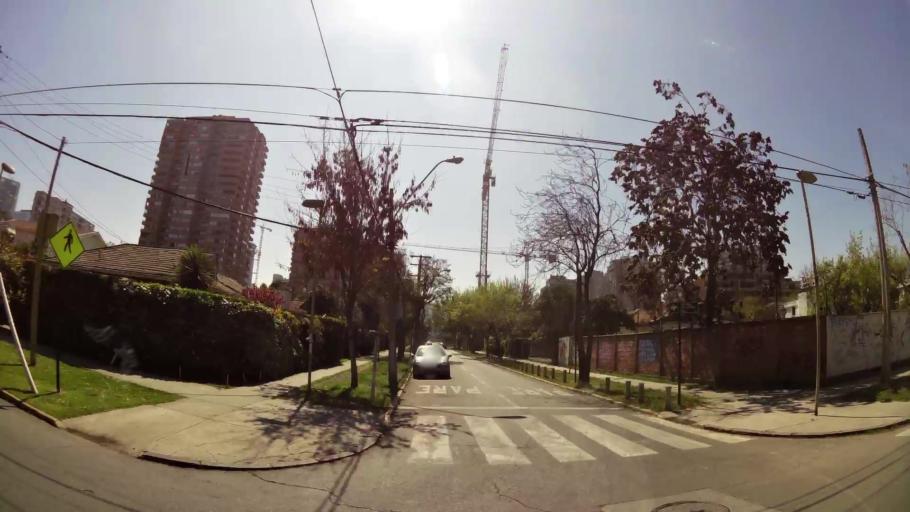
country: CL
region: Santiago Metropolitan
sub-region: Provincia de Santiago
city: Villa Presidente Frei, Nunoa, Santiago, Chile
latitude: -33.4128
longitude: -70.5699
